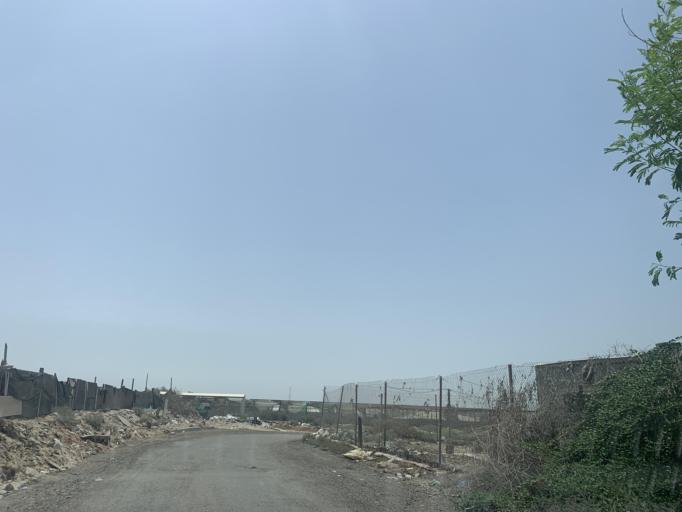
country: BH
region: Central Governorate
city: Madinat Hamad
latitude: 26.1549
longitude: 50.4936
